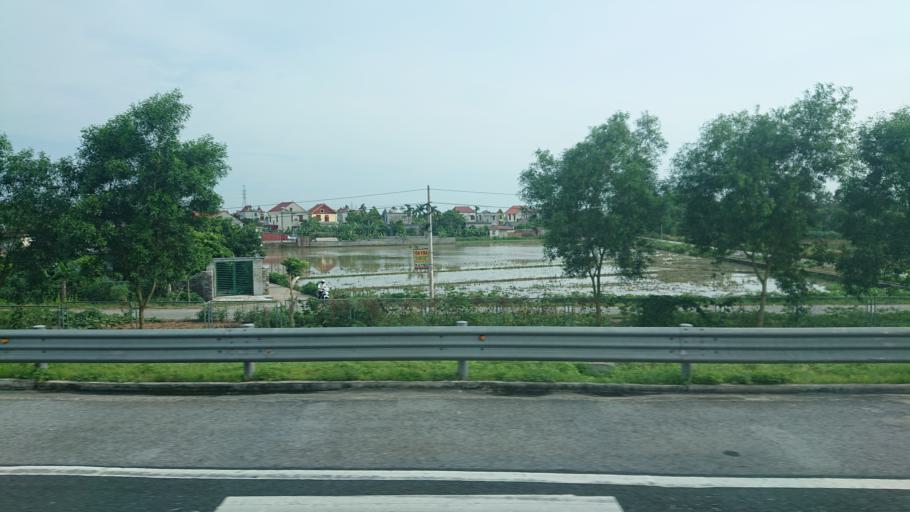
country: VN
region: Hai Phong
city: An Lao
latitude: 20.8044
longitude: 106.5215
